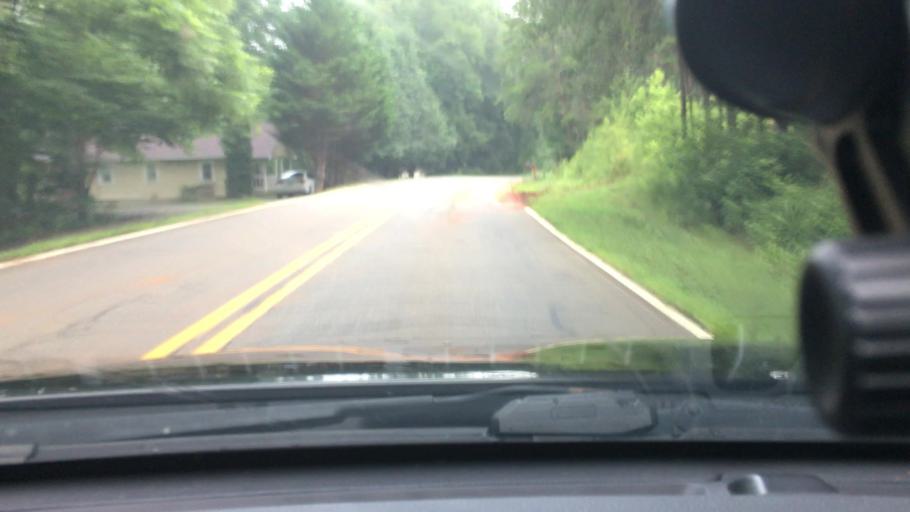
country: US
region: North Carolina
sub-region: Rutherford County
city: Rutherfordton
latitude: 35.3763
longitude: -81.9863
